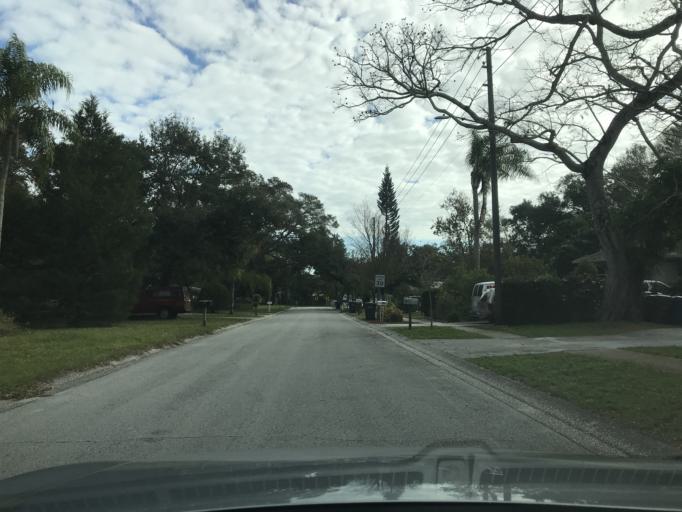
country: US
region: Florida
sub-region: Pinellas County
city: Largo
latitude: 27.9185
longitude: -82.7804
